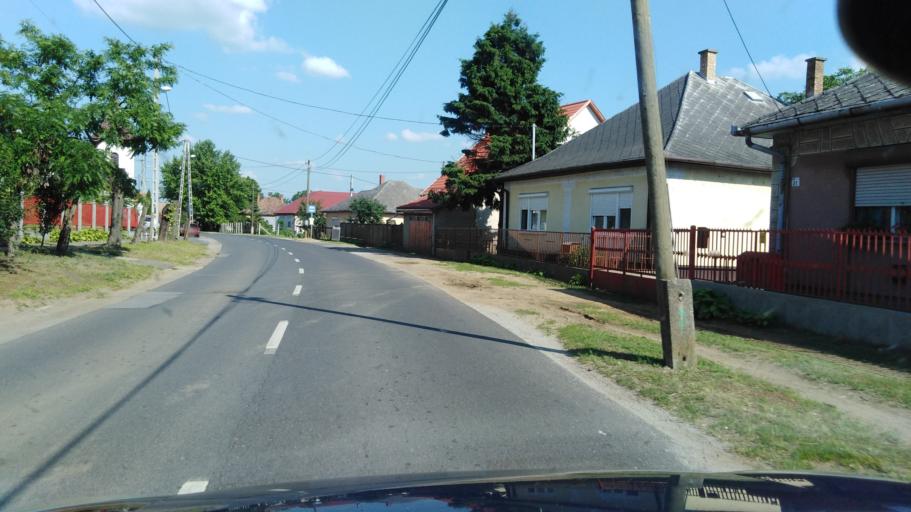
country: HU
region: Szabolcs-Szatmar-Bereg
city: Nyirvasvari
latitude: 47.8202
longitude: 22.1861
